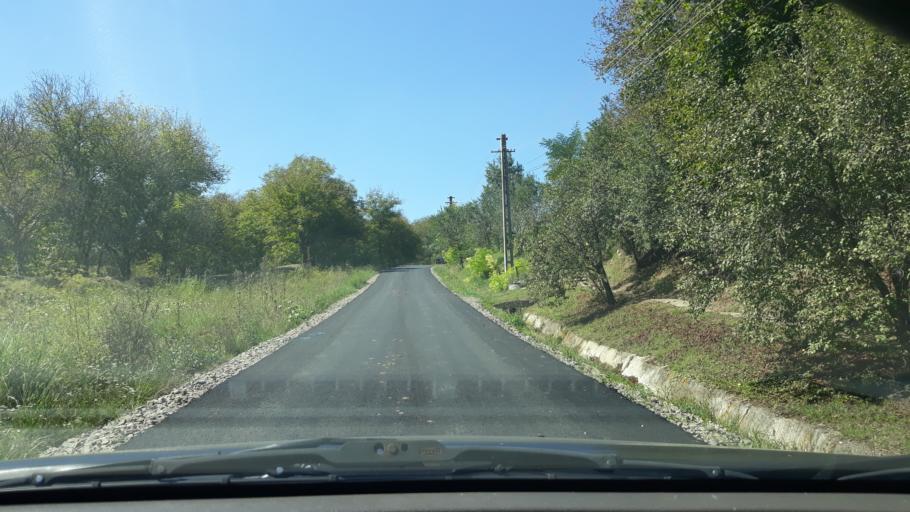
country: RO
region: Salaj
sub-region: Comuna Dobrin
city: Dobrin
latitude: 47.2900
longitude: 23.0942
